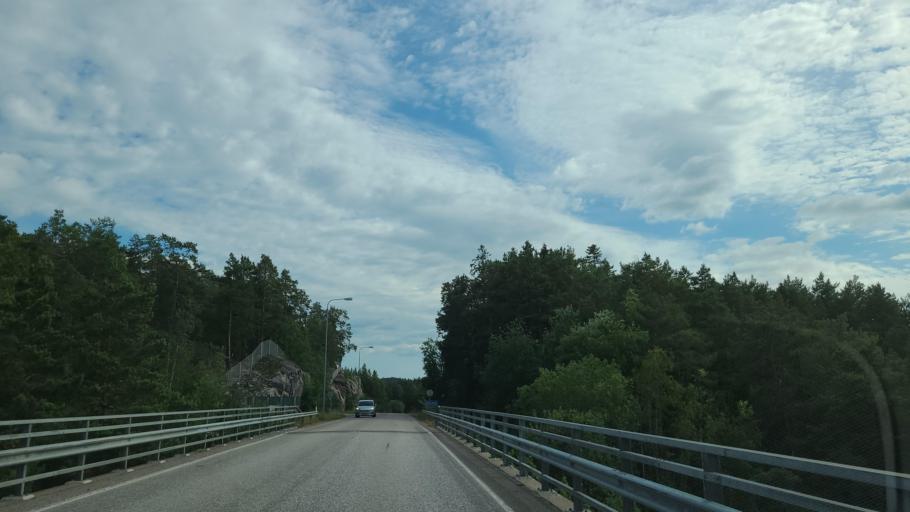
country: FI
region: Varsinais-Suomi
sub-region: Turku
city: Rymaettylae
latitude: 60.3362
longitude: 21.9797
